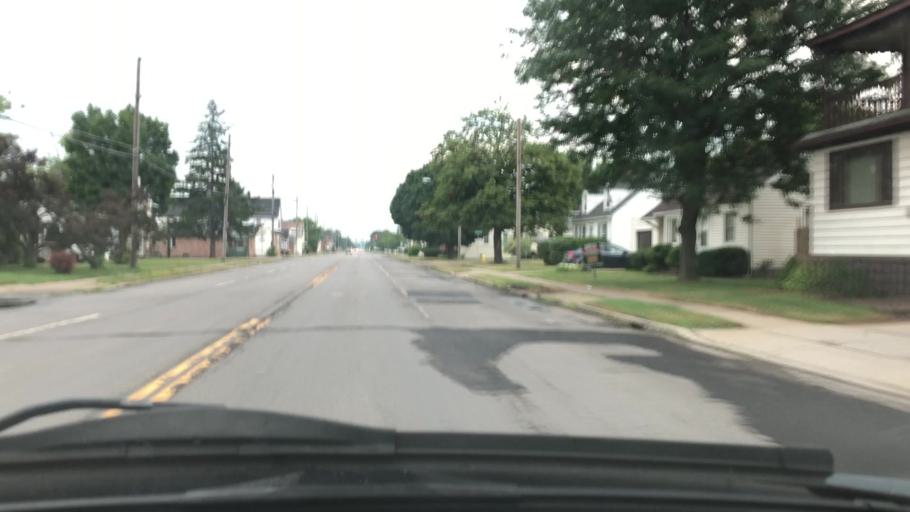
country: US
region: New York
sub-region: Erie County
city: Sloan
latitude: 42.8844
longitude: -78.7888
